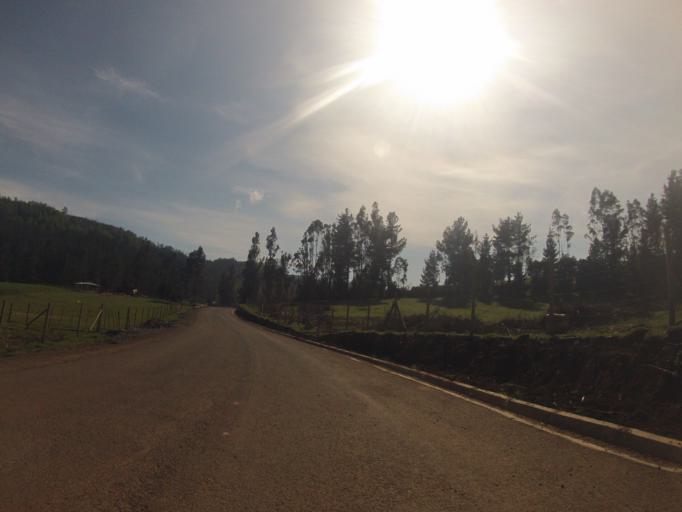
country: CL
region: Araucania
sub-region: Provincia de Cautin
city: Temuco
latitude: -38.6884
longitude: -72.5856
